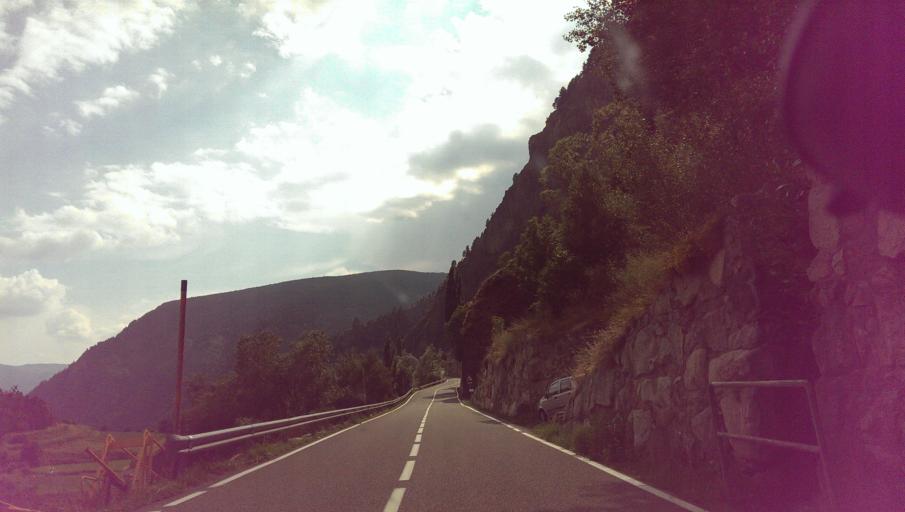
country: AD
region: Canillo
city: Canillo
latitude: 42.5664
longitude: 1.5940
